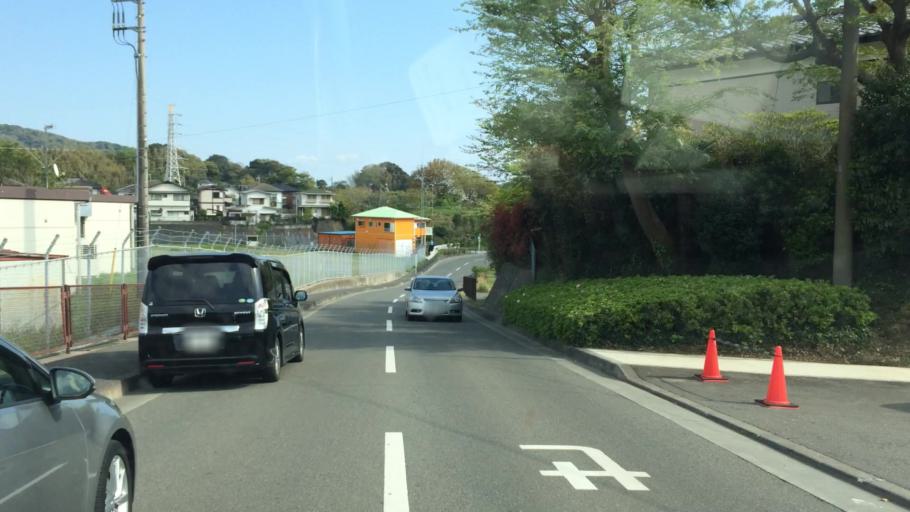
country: JP
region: Kanagawa
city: Yokosuka
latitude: 35.2323
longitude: 139.6297
